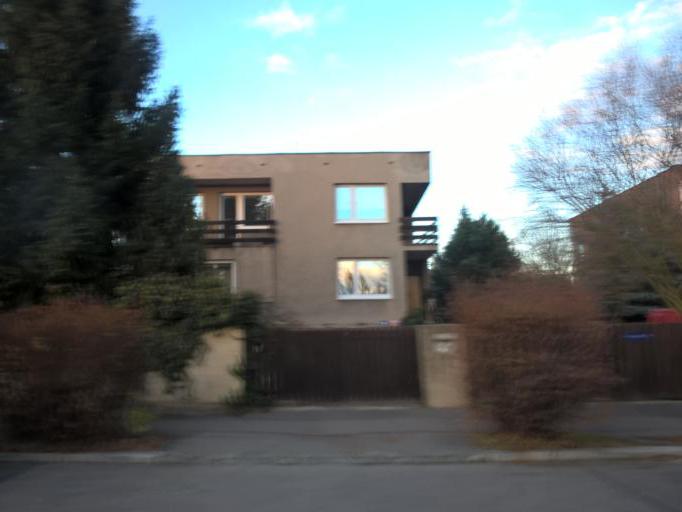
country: CZ
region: Praha
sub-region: Praha 1
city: Mala Strana
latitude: 50.0801
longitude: 14.3712
